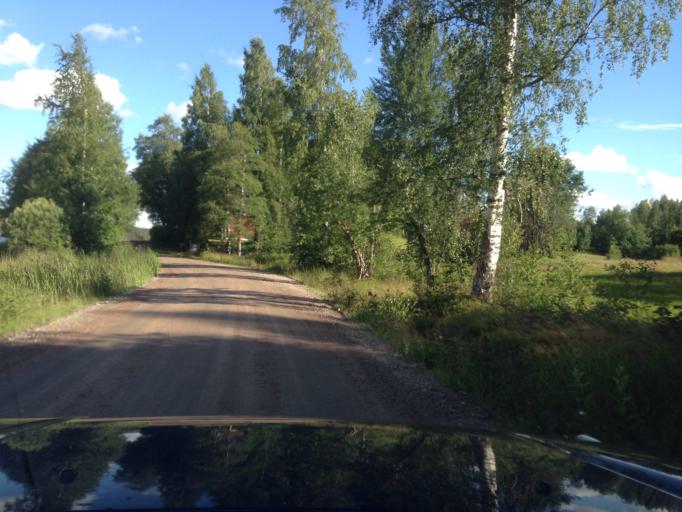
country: SE
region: Dalarna
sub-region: Ludvika Kommun
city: Abborrberget
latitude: 60.2762
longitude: 14.7268
